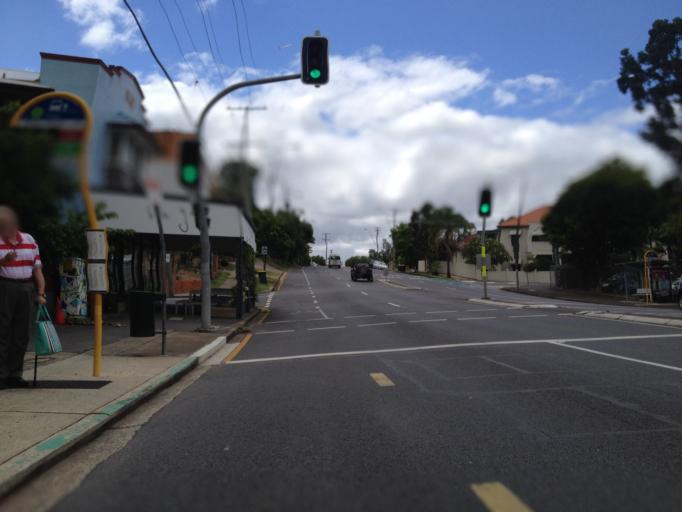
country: AU
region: Queensland
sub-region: Brisbane
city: South Brisbane
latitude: -27.4941
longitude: 153.0230
